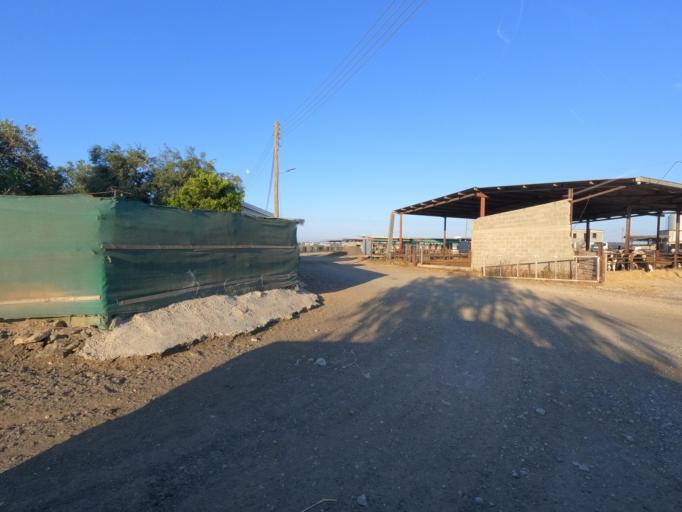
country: CY
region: Ammochostos
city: Achna
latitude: 35.0346
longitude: 33.7892
